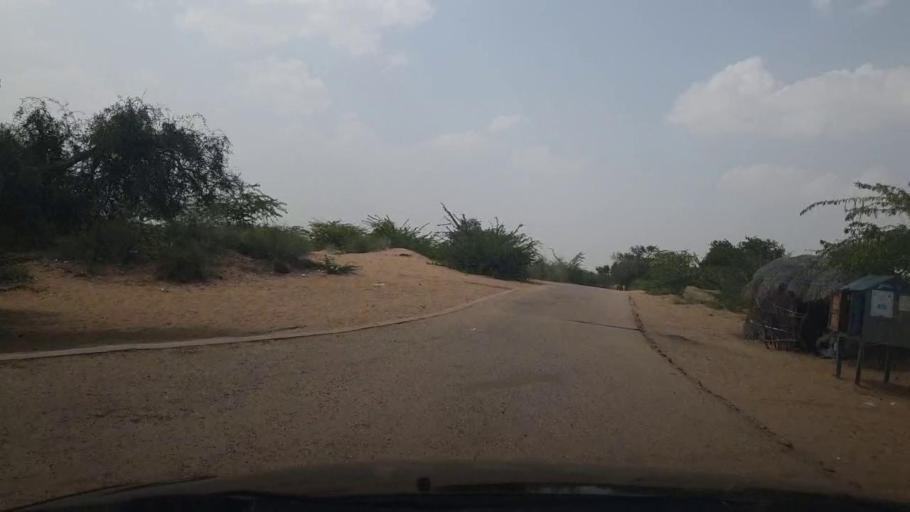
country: PK
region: Sindh
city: Islamkot
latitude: 24.9934
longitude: 70.4955
